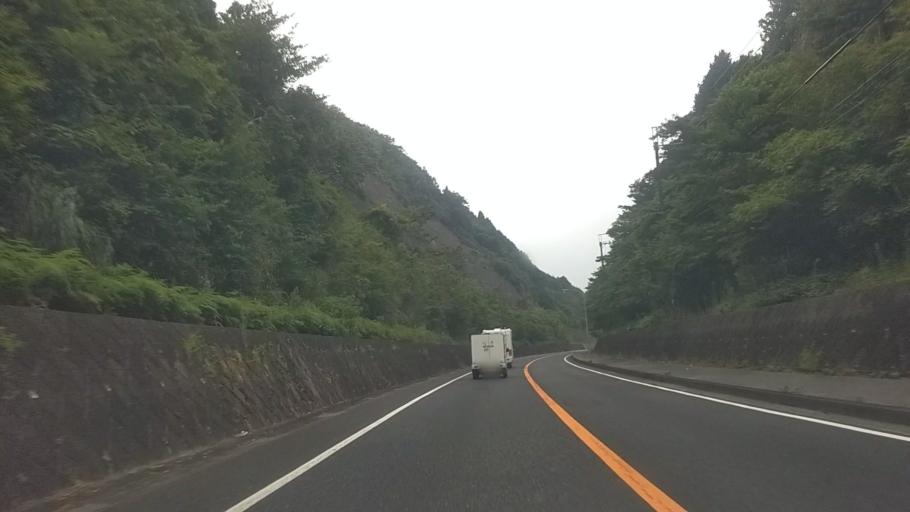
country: JP
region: Chiba
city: Kawaguchi
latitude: 35.1818
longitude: 140.0616
